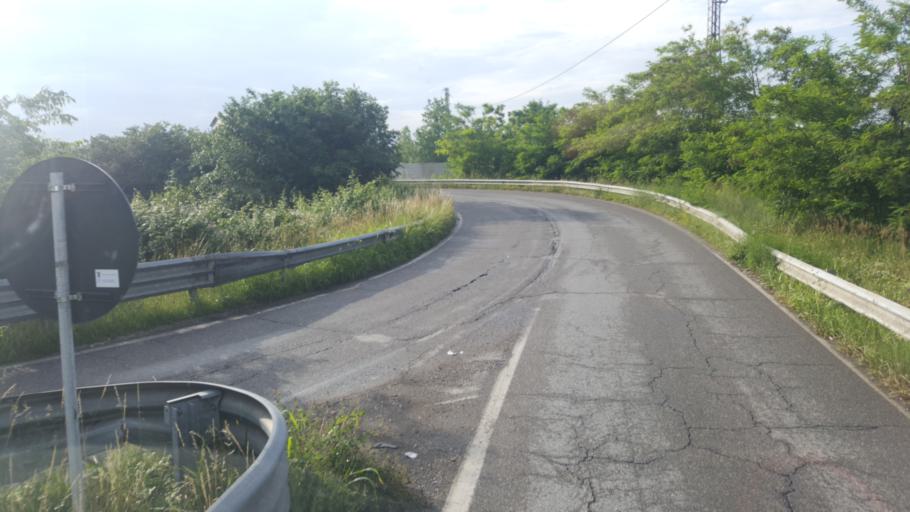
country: IT
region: Lombardy
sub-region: Provincia di Brescia
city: Molinetto
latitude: 45.4832
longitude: 10.3725
